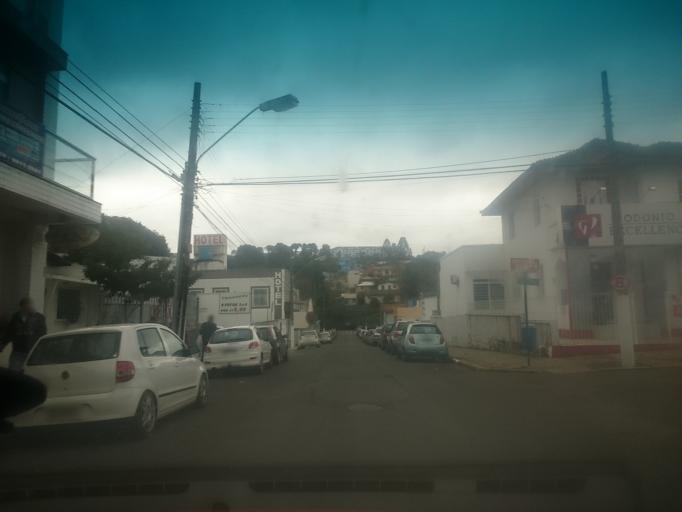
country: BR
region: Santa Catarina
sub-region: Lages
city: Lages
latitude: -27.8124
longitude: -50.3290
